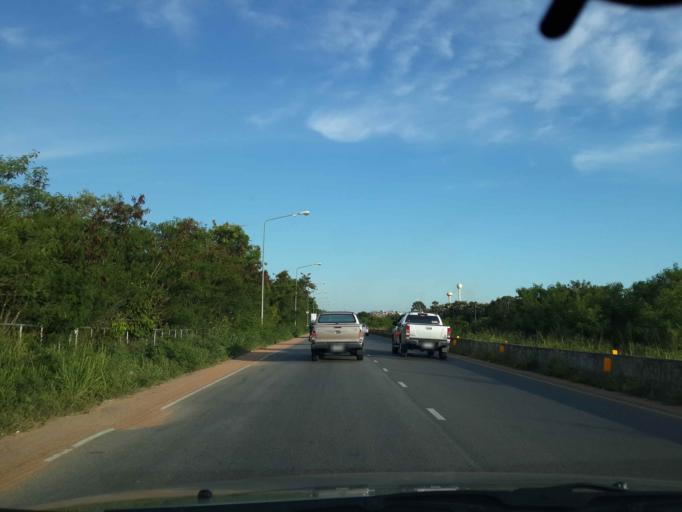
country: TH
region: Chon Buri
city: Phatthaya
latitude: 12.8893
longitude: 100.9017
